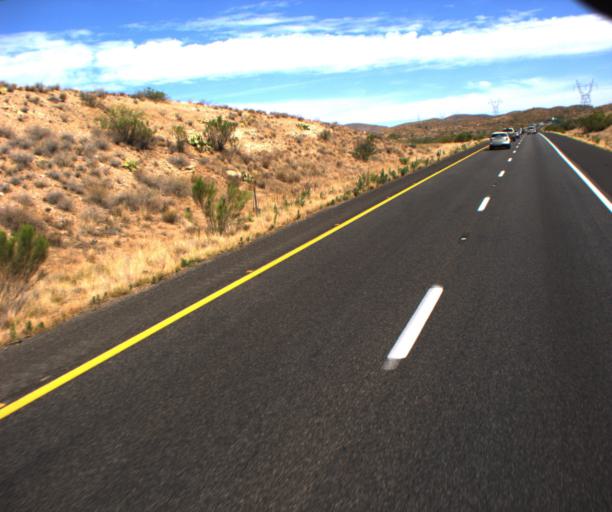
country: US
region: Arizona
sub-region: Yavapai County
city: Cordes Lakes
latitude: 34.2479
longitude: -112.1122
